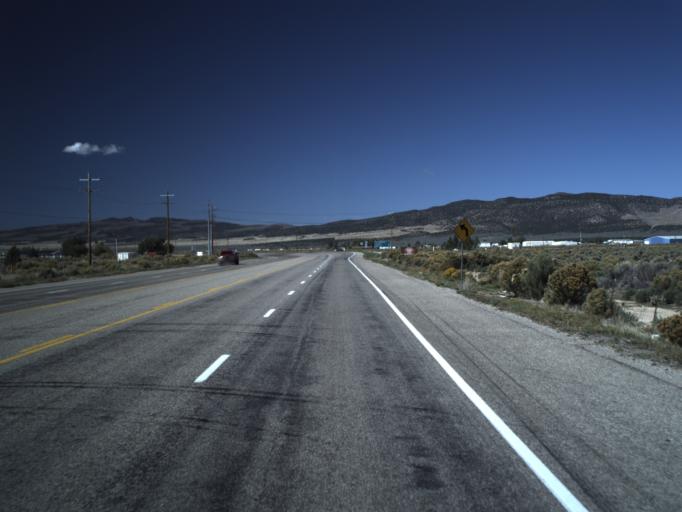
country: US
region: Utah
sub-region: Iron County
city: Cedar City
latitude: 37.6850
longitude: -113.1575
